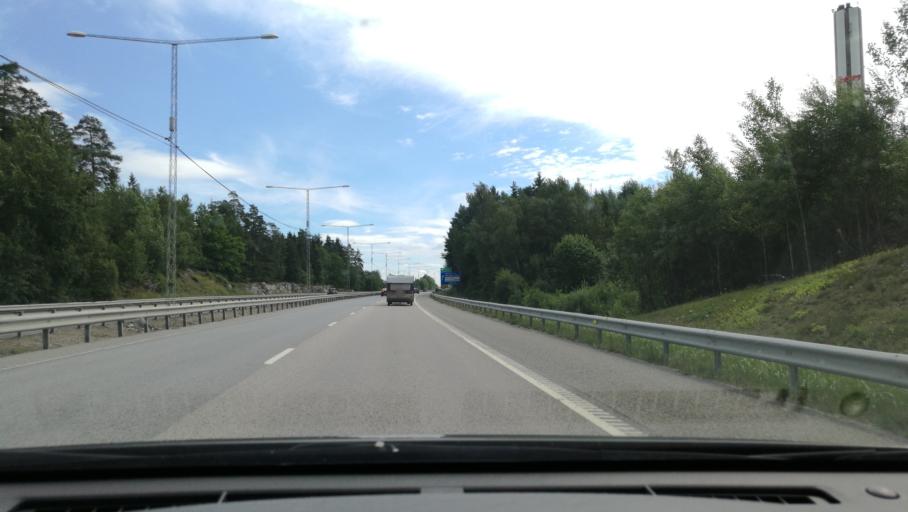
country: SE
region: Stockholm
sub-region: Jarfalla Kommun
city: Jakobsberg
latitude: 59.4288
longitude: 17.8490
